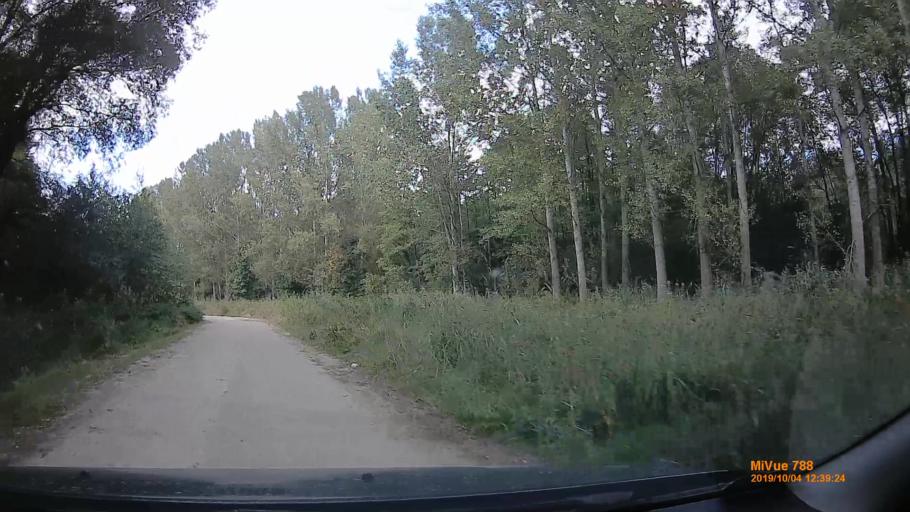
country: HU
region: Somogy
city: Karad
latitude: 46.6735
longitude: 17.7804
